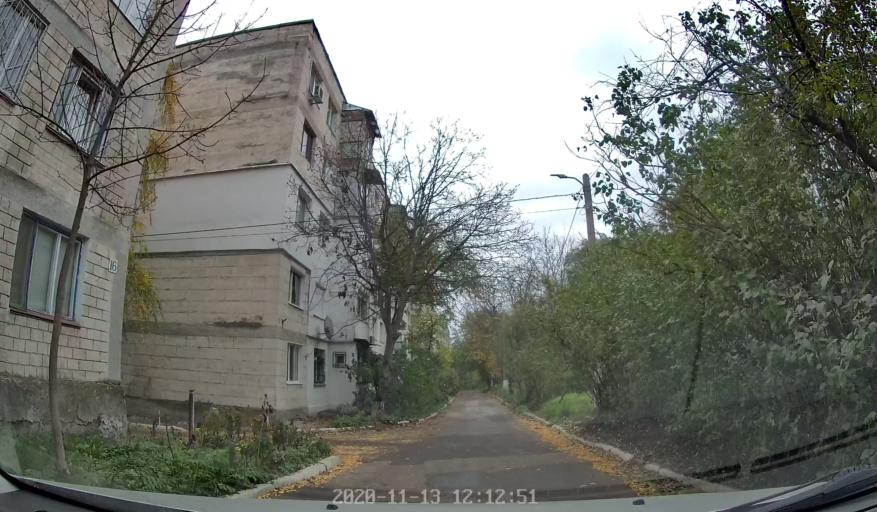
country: MD
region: Chisinau
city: Chisinau
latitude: 46.9546
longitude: 28.8368
